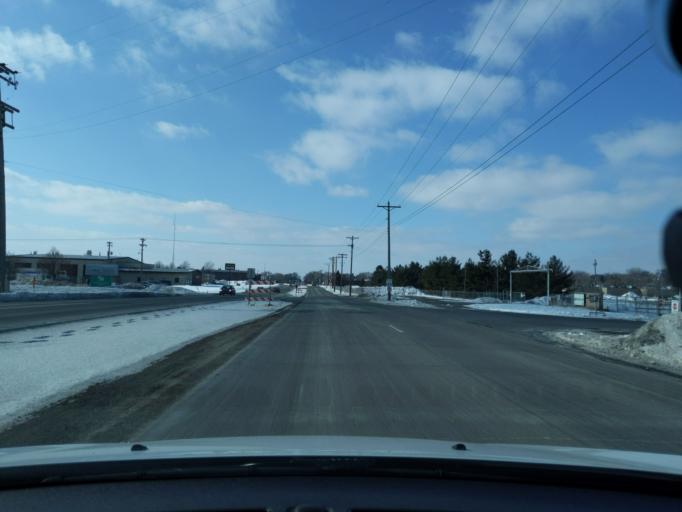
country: US
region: Minnesota
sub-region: Hennepin County
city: Saint Anthony
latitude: 45.0207
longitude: -93.2024
